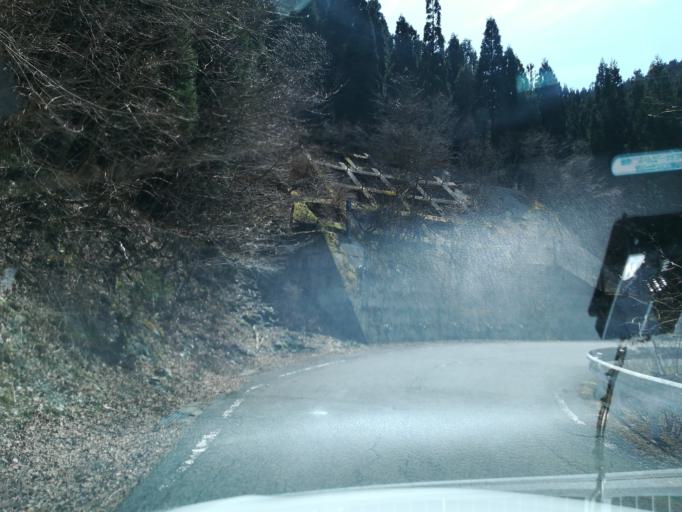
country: JP
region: Tokushima
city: Wakimachi
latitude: 33.8804
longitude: 134.0554
